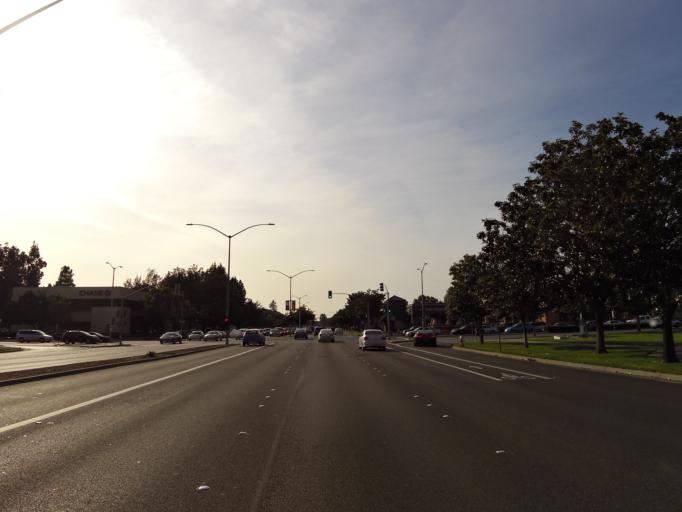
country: US
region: California
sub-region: Alameda County
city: Fremont
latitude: 37.5516
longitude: -121.9771
